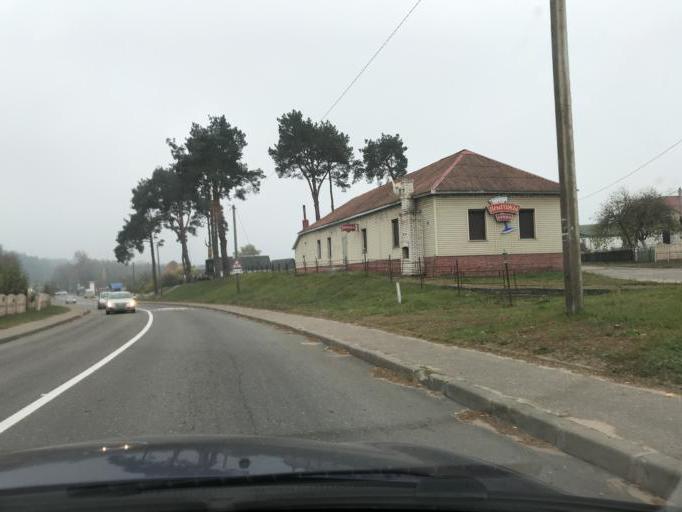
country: BY
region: Grodnenskaya
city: Hrodna
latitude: 53.8142
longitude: 23.8608
